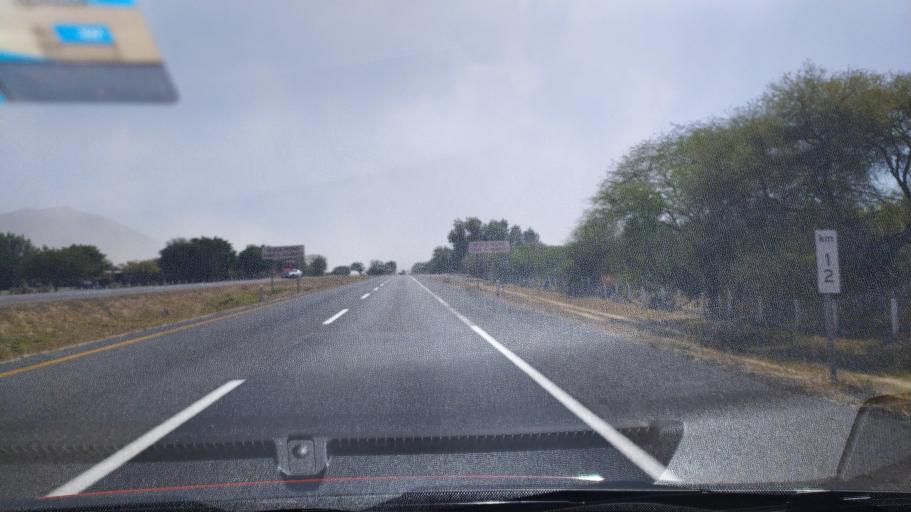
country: MX
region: Jalisco
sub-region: Acatlan de Juarez
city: Villa de los Ninos
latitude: 20.3351
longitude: -103.5702
